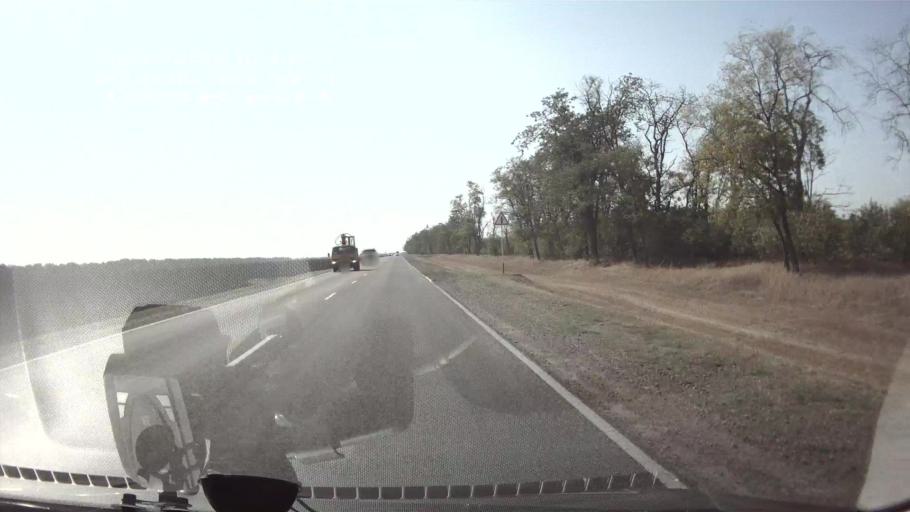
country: RU
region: Krasnodarskiy
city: Belaya Glina
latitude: 46.0438
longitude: 40.7988
